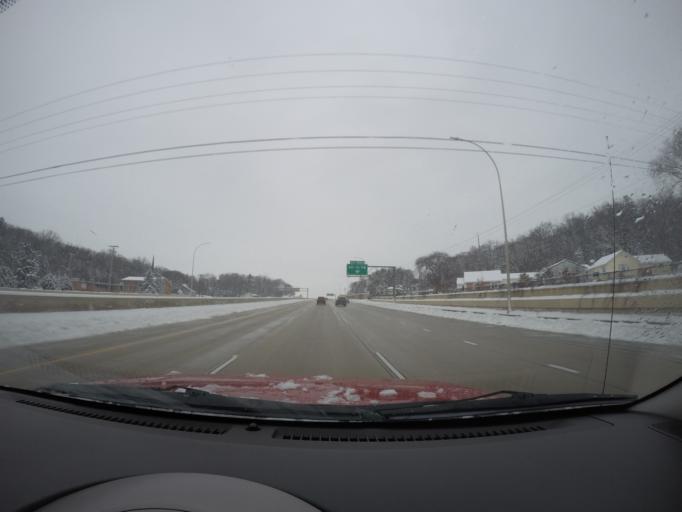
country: US
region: Minnesota
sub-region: Olmsted County
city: Rochester
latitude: 44.0103
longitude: -92.4829
